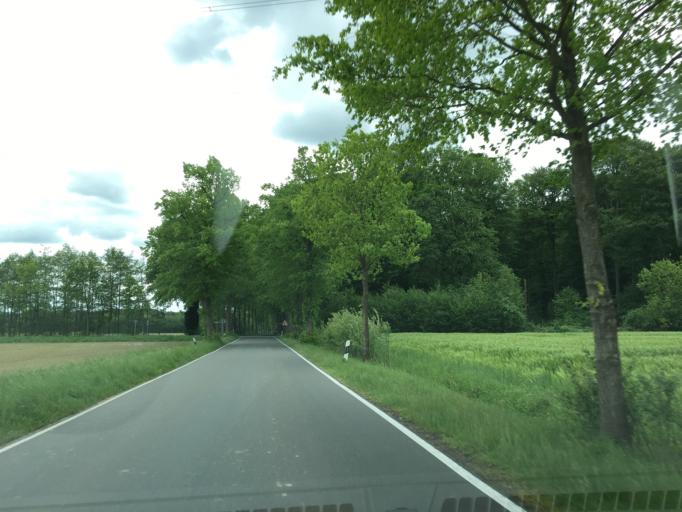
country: DE
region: North Rhine-Westphalia
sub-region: Regierungsbezirk Munster
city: Senden
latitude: 51.9433
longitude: 7.5115
